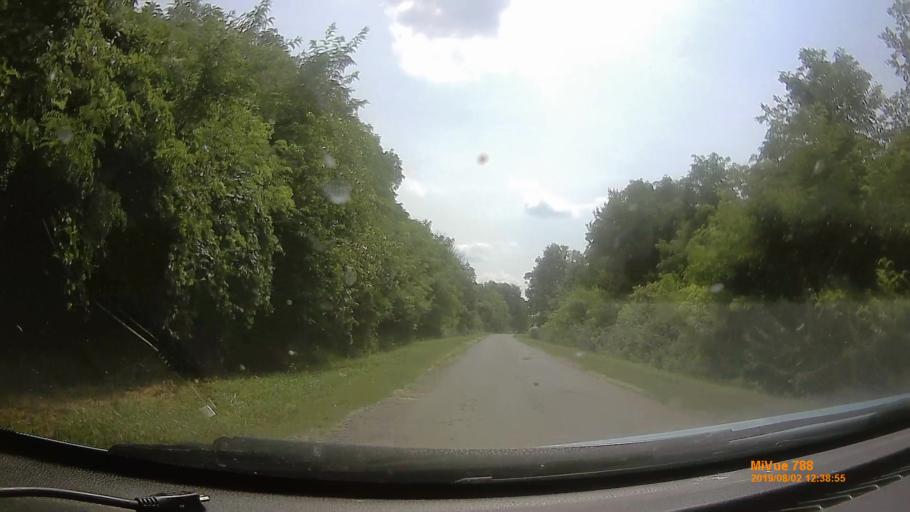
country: HU
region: Baranya
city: Buekkoesd
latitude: 46.0931
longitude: 17.9578
